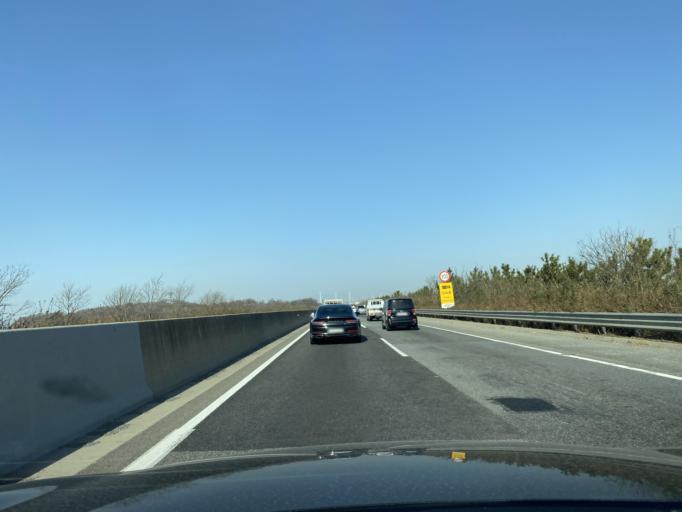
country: KR
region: Gyeonggi-do
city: Ansan-si
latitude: 37.2703
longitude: 126.7460
